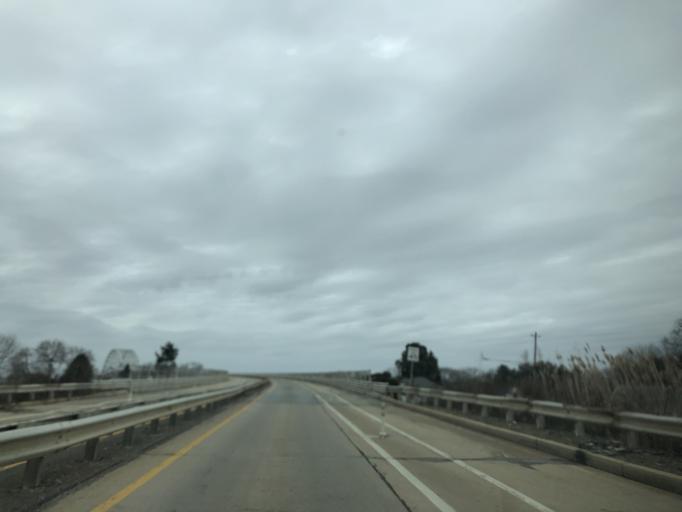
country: US
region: Delaware
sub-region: New Castle County
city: Delaware City
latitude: 39.5468
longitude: -75.6486
